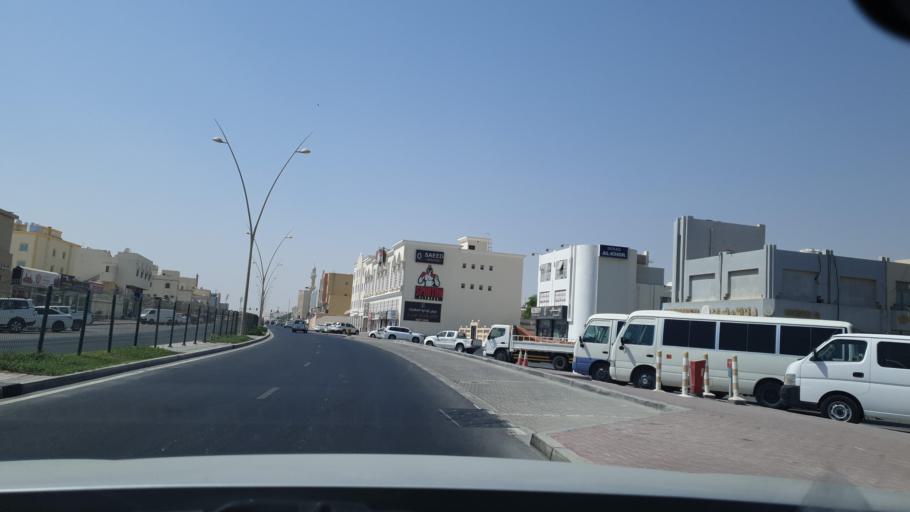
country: QA
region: Al Khawr
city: Al Khawr
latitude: 25.6842
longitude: 51.5062
